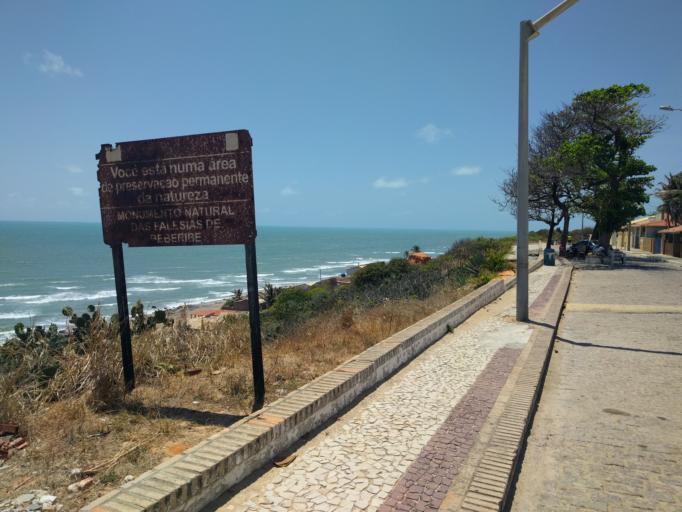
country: BR
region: Ceara
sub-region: Beberibe
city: Beberibe
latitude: -4.1546
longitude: -38.1108
